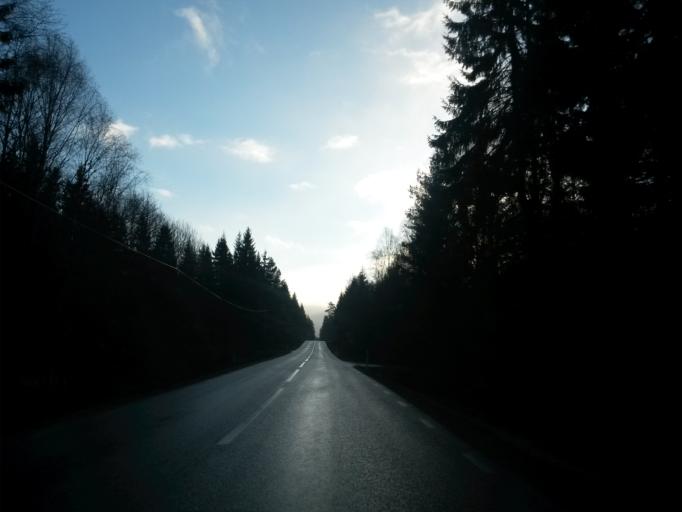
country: SE
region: Vaestra Goetaland
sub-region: Boras Kommun
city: Boras
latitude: 57.8812
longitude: 12.9283
